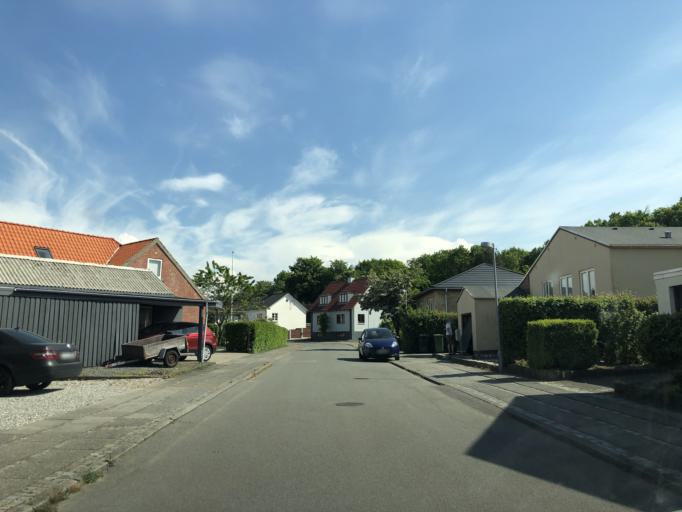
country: DK
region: Central Jutland
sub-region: Holstebro Kommune
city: Holstebro
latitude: 56.3565
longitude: 8.6050
